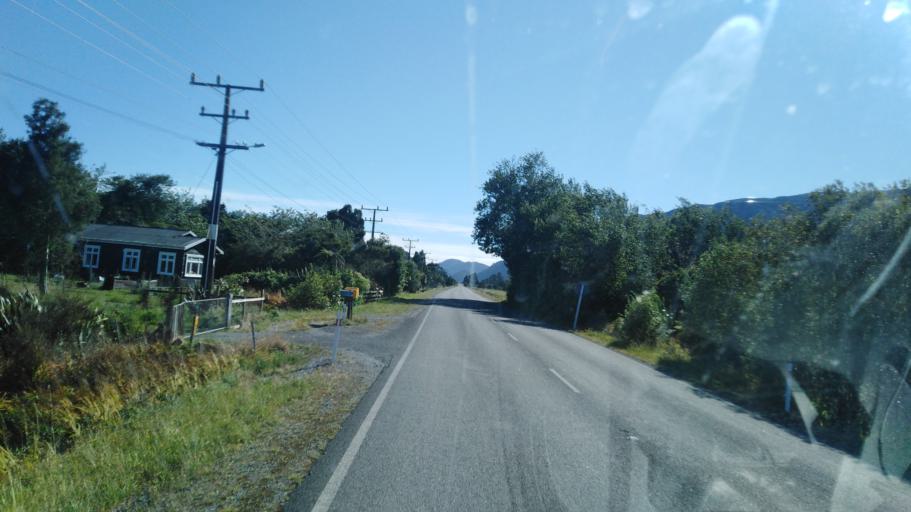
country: NZ
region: West Coast
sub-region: Buller District
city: Westport
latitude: -41.6766
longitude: 171.7976
